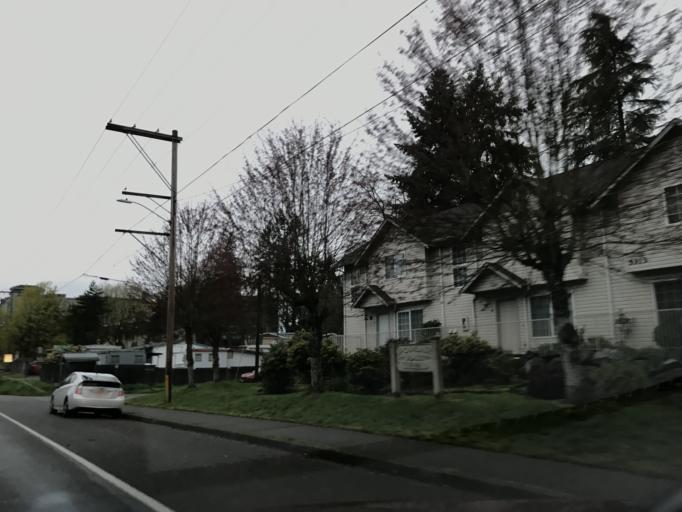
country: US
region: Washington
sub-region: Snohomish County
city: Mountlake Terrace
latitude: 47.7775
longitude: -122.3048
